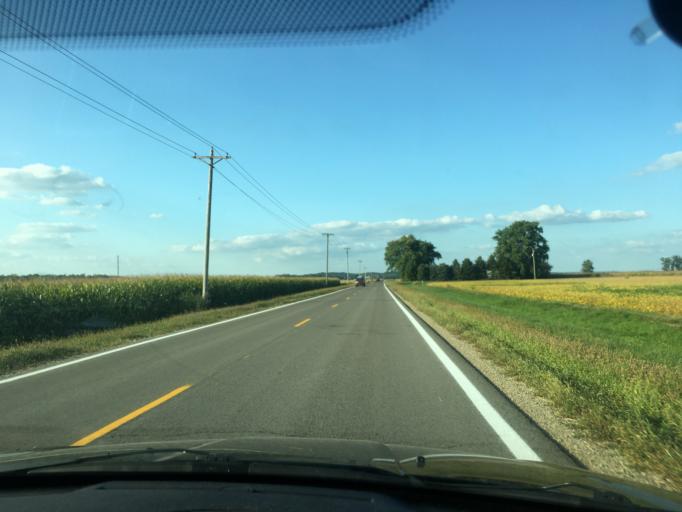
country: US
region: Ohio
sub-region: Logan County
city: West Liberty
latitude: 40.1919
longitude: -83.7812
